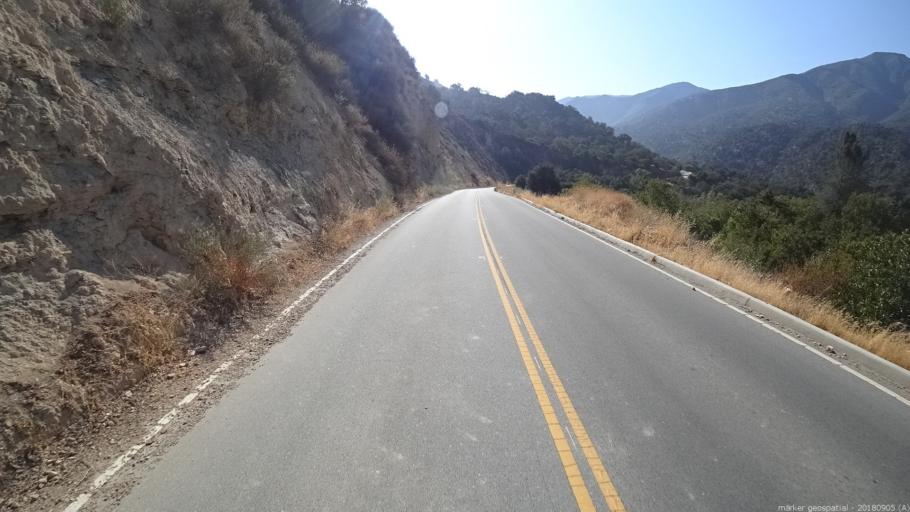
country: US
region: California
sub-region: Monterey County
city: Soledad
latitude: 36.2358
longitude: -121.4701
